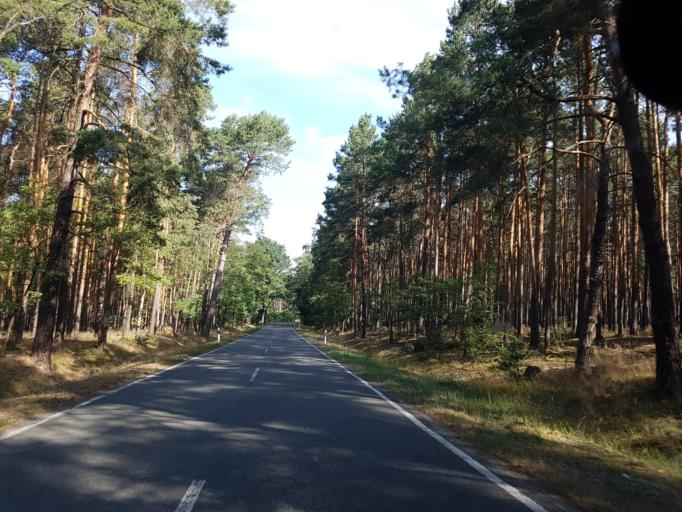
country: DE
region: Brandenburg
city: Ihlow
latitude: 51.9766
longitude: 13.3038
